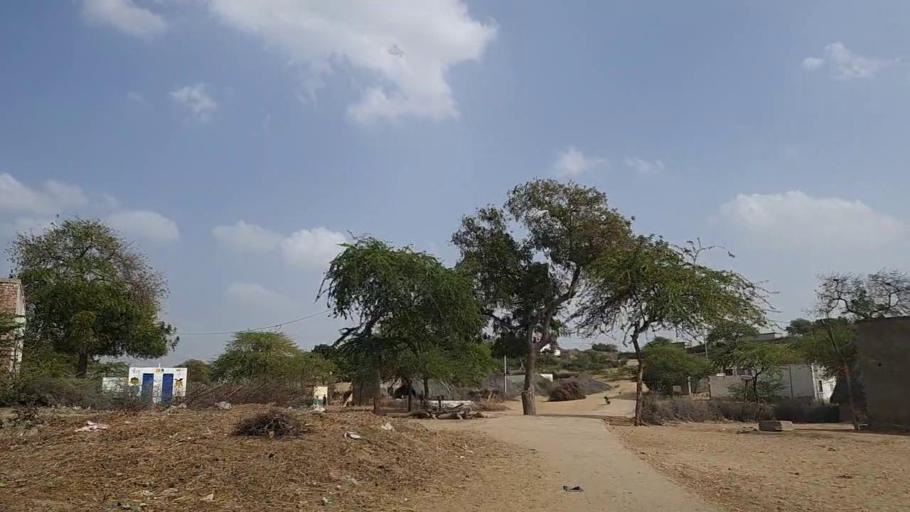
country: PK
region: Sindh
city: Islamkot
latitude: 24.8277
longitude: 70.1858
